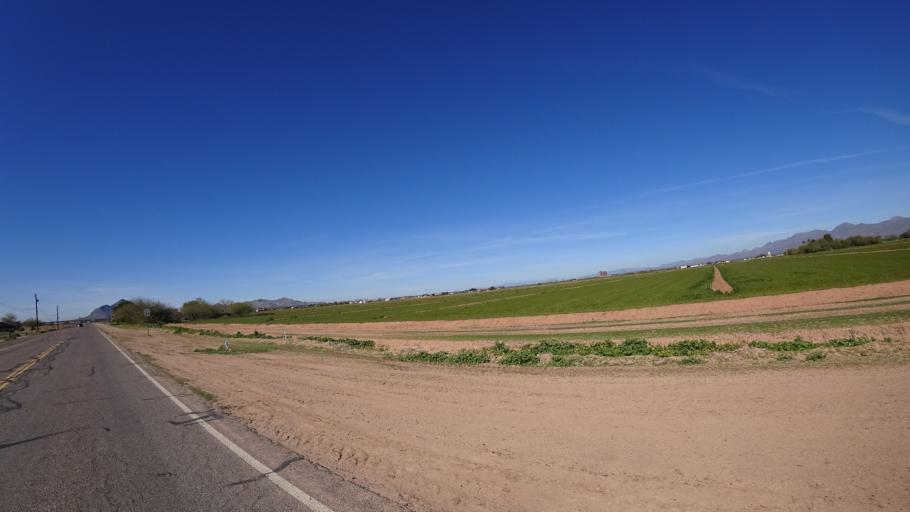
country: US
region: Arizona
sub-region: Maricopa County
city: Scottsdale
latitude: 33.5096
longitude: -111.8583
